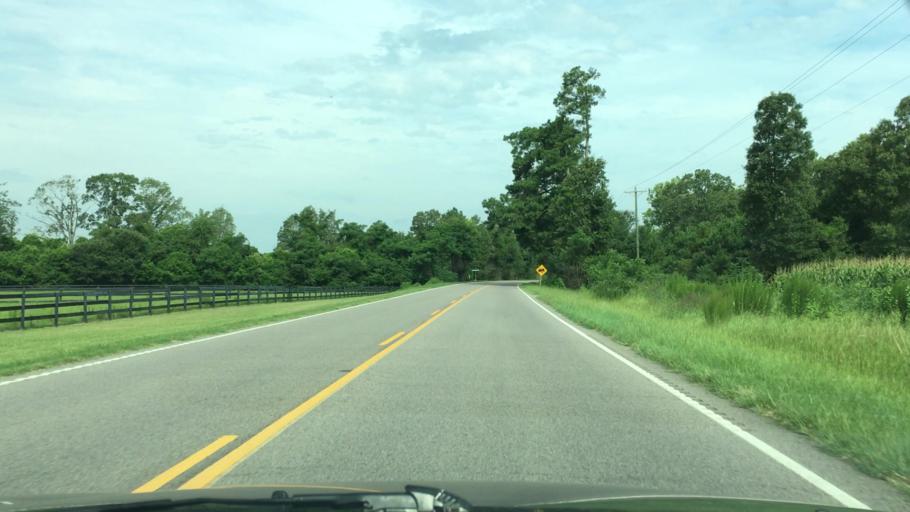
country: US
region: South Carolina
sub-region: Lexington County
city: Batesburg-Leesville
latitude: 33.6897
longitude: -81.4689
